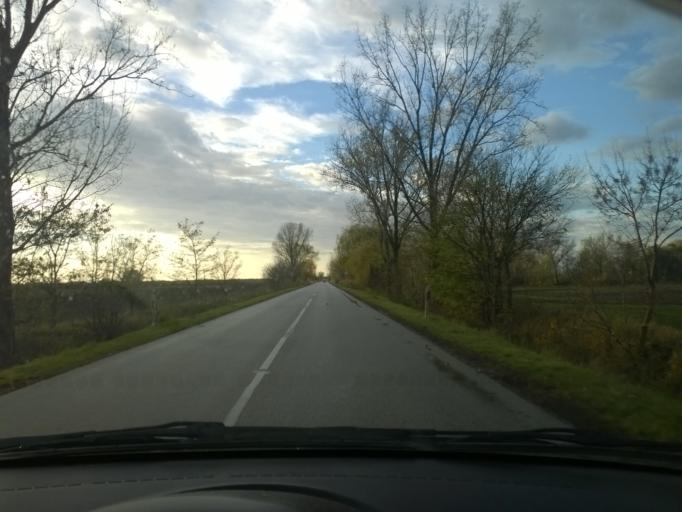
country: HU
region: Bacs-Kiskun
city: Kalocsa
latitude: 46.5079
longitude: 19.0332
